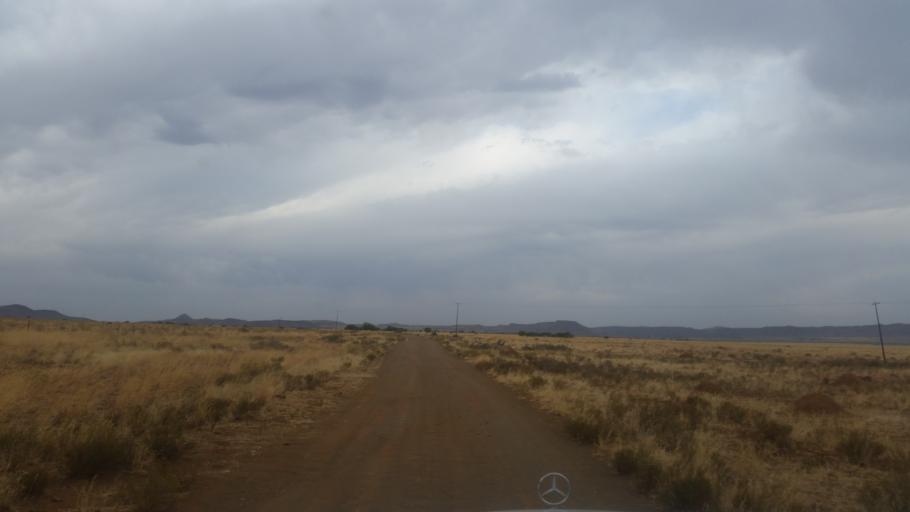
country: ZA
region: Orange Free State
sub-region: Xhariep District Municipality
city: Trompsburg
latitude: -30.5069
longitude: 25.9377
